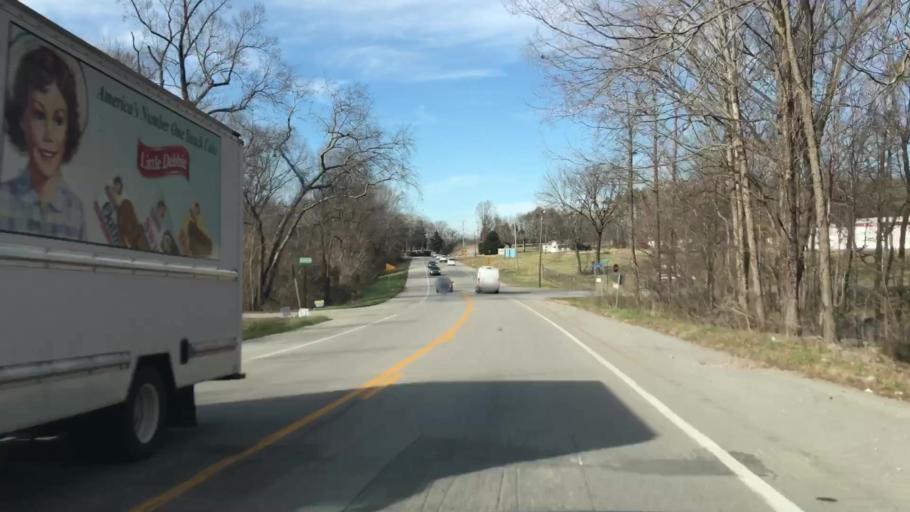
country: US
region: Kentucky
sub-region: Pulaski County
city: Somerset
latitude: 36.9702
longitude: -84.5894
